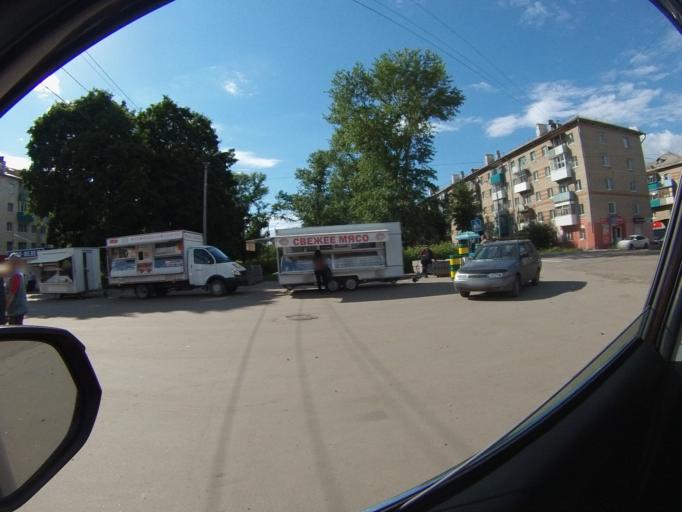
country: RU
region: Orjol
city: Mtsensk
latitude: 53.2746
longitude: 36.5753
